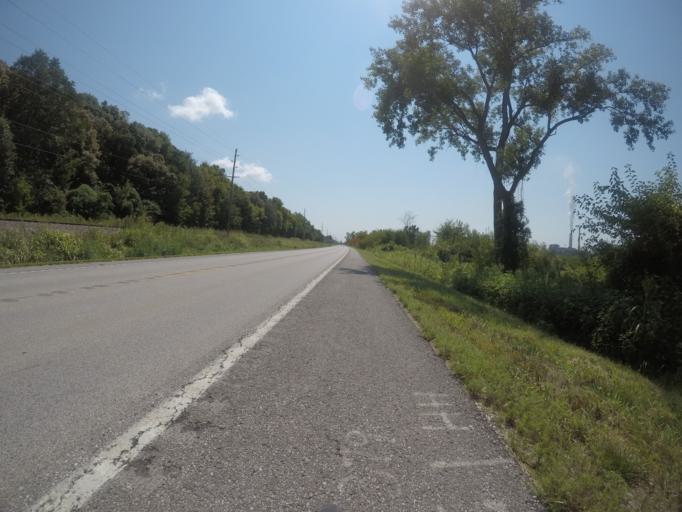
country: US
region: Missouri
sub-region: Platte County
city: Weston
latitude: 39.4688
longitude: -94.9790
